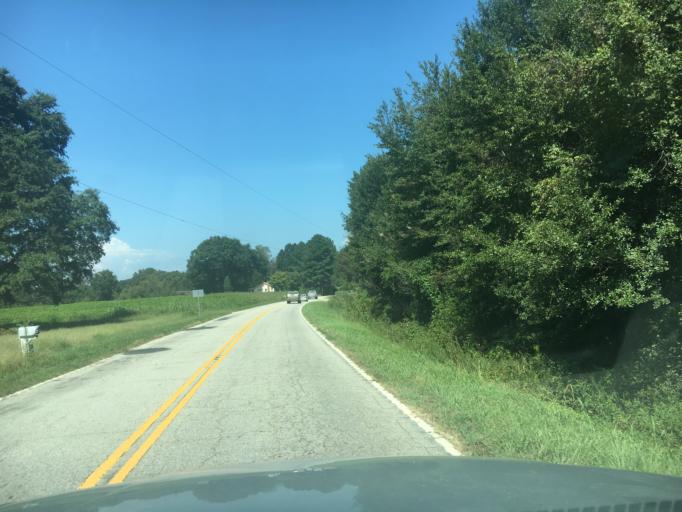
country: US
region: South Carolina
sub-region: Spartanburg County
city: Landrum
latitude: 35.1855
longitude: -82.0443
